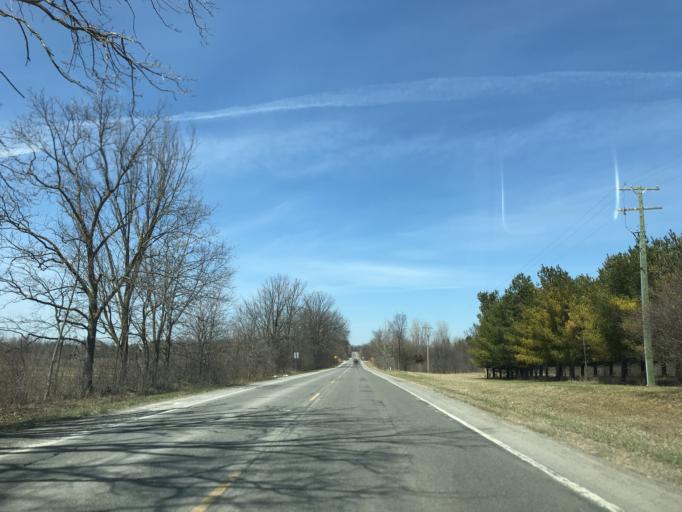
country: US
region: Michigan
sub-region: Washtenaw County
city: Ann Arbor
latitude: 42.3286
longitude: -83.7080
